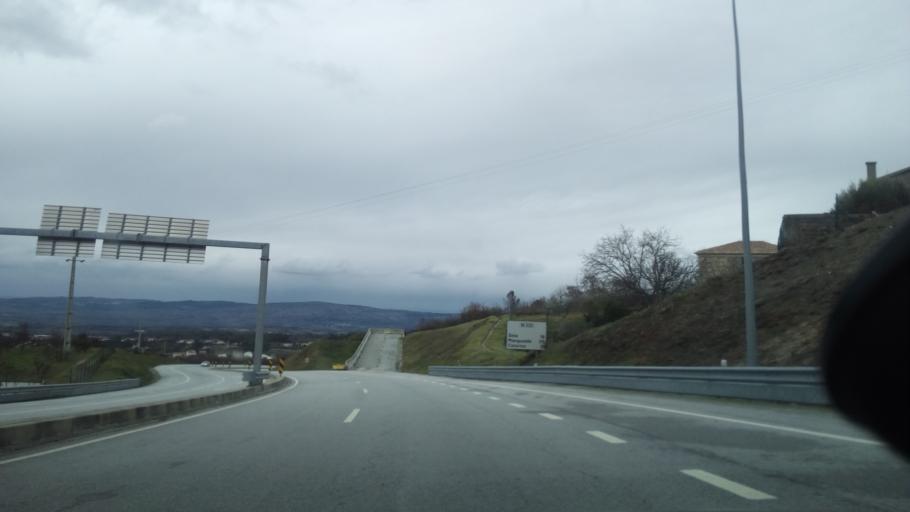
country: PT
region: Guarda
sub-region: Manteigas
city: Manteigas
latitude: 40.4872
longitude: -7.5989
